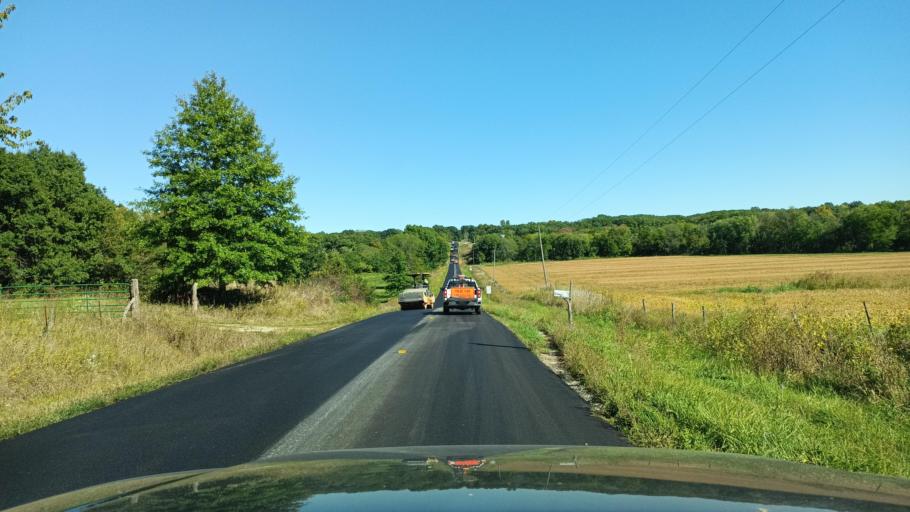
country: US
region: Missouri
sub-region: Macon County
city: La Plata
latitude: 39.9196
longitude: -92.5224
